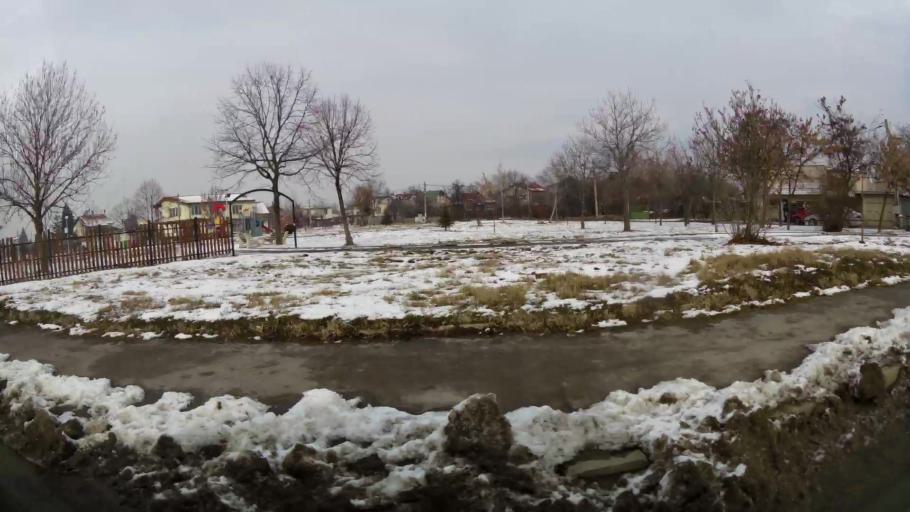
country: BG
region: Sofia-Capital
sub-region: Stolichna Obshtina
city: Sofia
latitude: 42.7119
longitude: 23.4085
